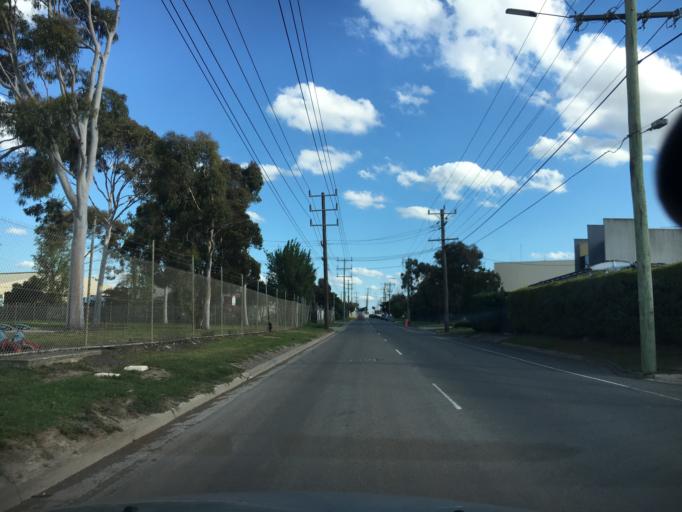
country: AU
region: Victoria
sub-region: Monash
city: Clayton
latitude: -37.9232
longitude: 145.1459
